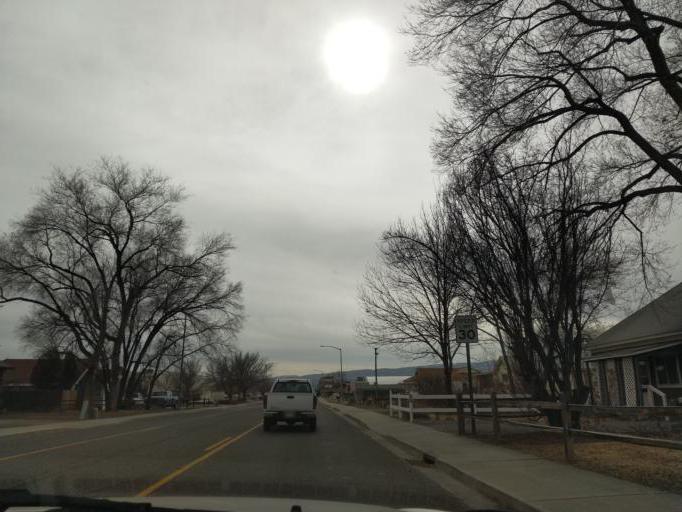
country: US
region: Colorado
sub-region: Mesa County
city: Grand Junction
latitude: 39.0803
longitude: -108.5292
